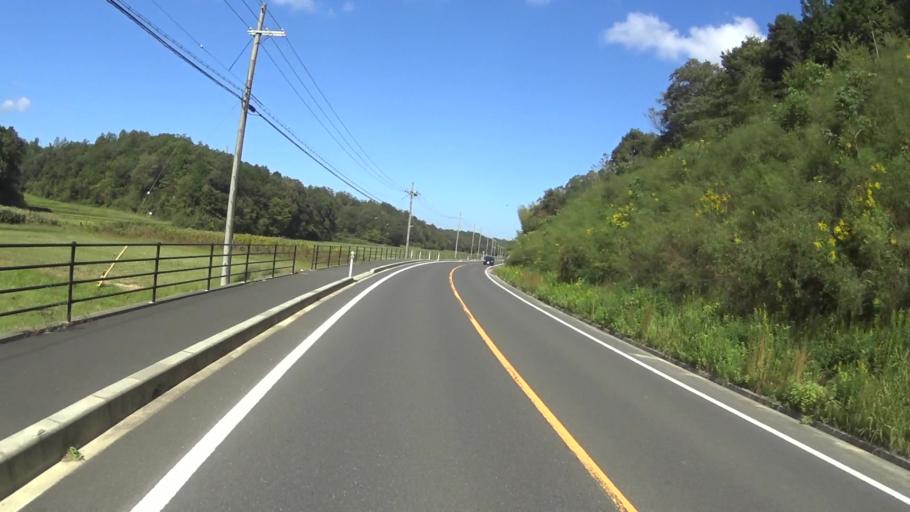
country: JP
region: Kyoto
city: Miyazu
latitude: 35.6440
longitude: 135.0712
